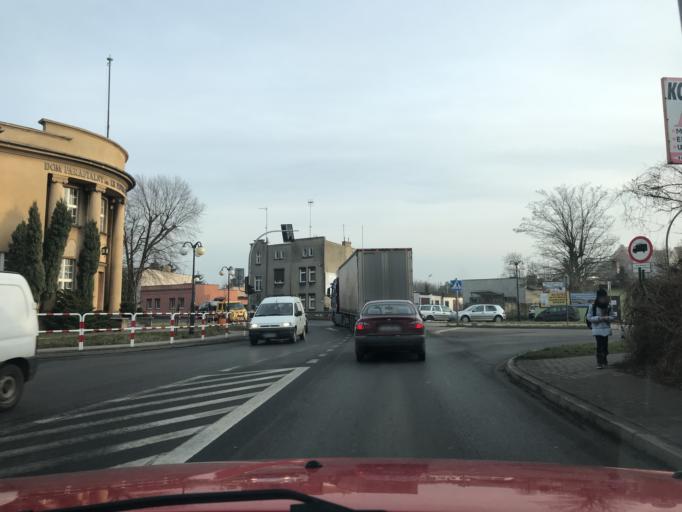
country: PL
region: Greater Poland Voivodeship
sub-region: Powiat pleszewski
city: Pleszew
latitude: 51.8987
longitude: 17.7888
